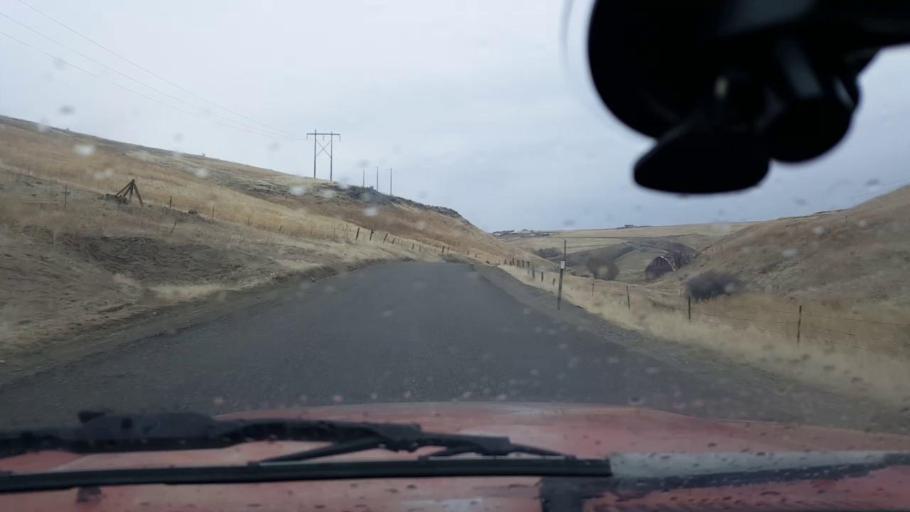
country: US
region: Washington
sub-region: Asotin County
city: Clarkston Heights-Vineland
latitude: 46.3894
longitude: -117.1404
